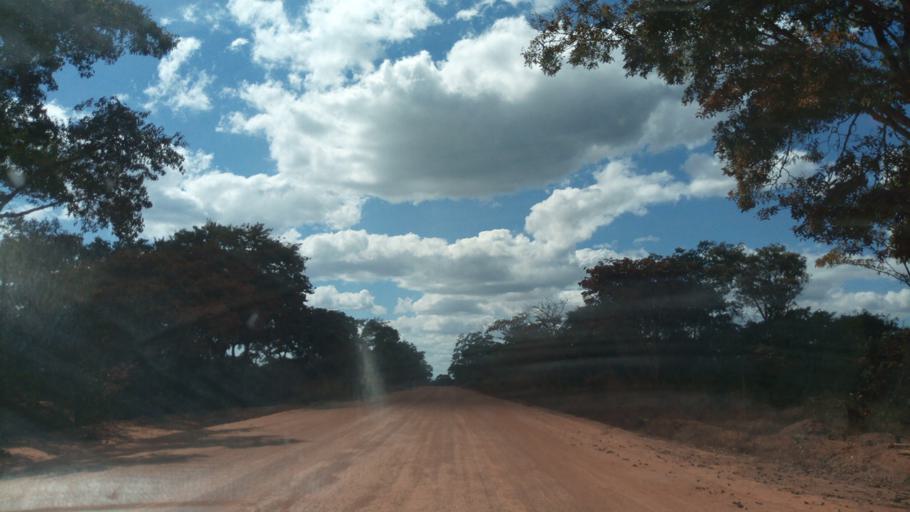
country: ZM
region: Copperbelt
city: Mufulira
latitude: -12.0363
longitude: 28.6700
